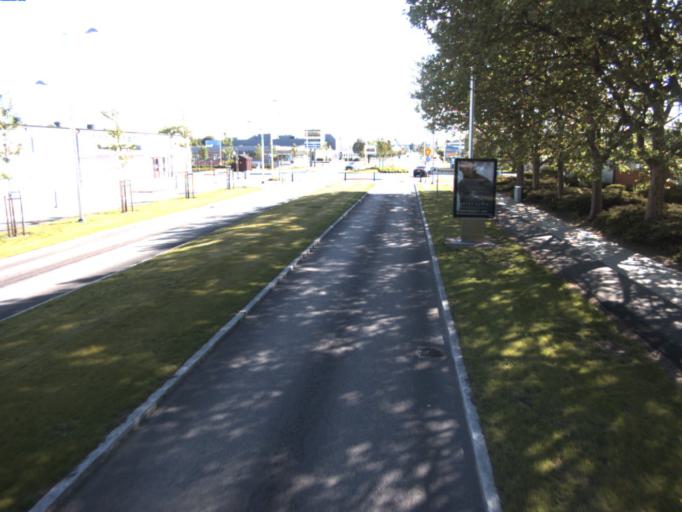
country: SE
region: Skane
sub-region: Helsingborg
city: Odakra
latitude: 56.0731
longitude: 12.7260
